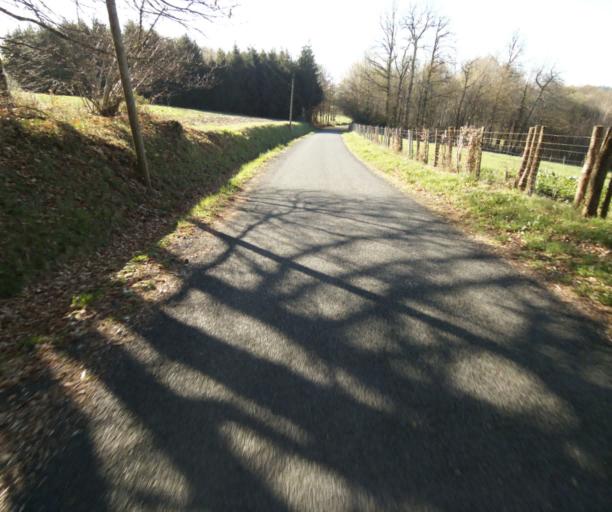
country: FR
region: Limousin
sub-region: Departement de la Correze
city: Seilhac
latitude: 45.3699
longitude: 1.7523
